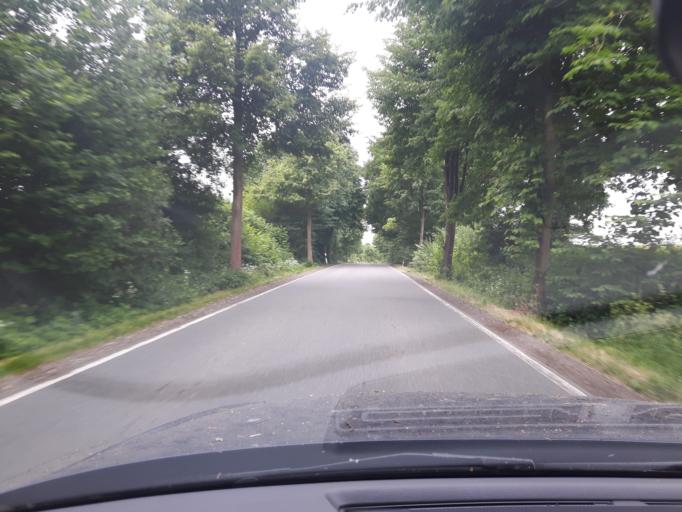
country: DE
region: Schleswig-Holstein
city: Ratekau
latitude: 53.9508
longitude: 10.7566
